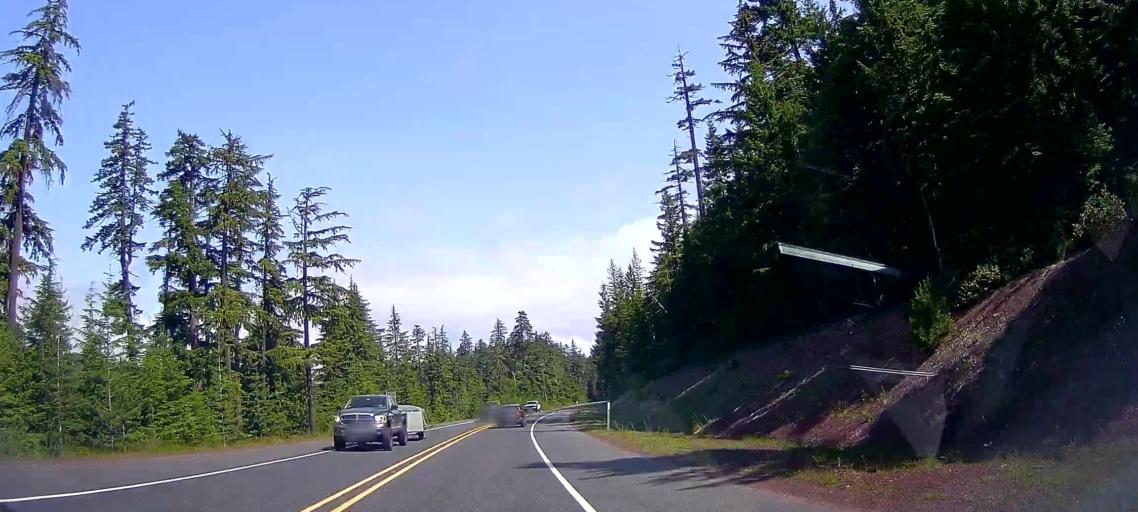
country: US
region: Oregon
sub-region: Clackamas County
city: Mount Hood Village
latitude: 45.1971
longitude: -121.6921
